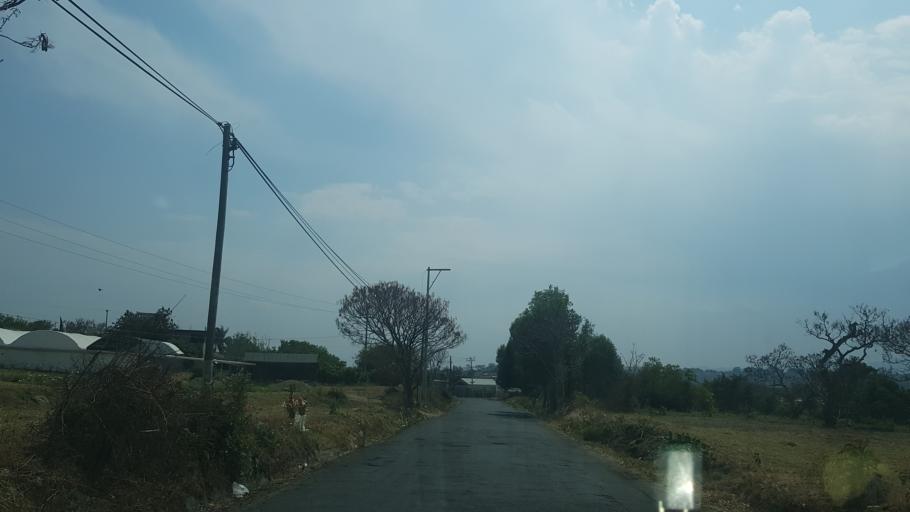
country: MX
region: Puebla
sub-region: Tianguismanalco
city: San Martin Tlapala
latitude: 18.9685
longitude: -98.4562
